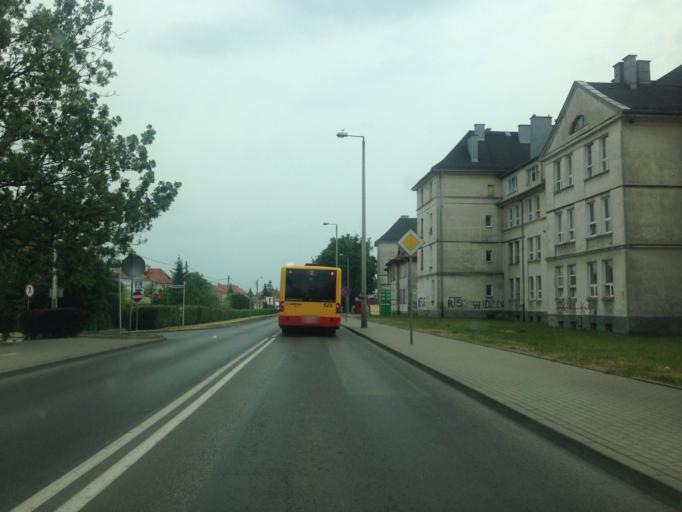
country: PL
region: Kujawsko-Pomorskie
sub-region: Grudziadz
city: Grudziadz
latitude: 53.4991
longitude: 18.7772
